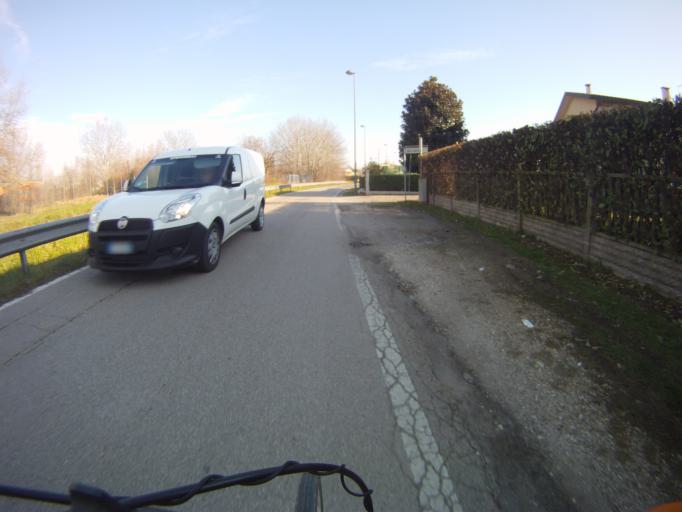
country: IT
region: Veneto
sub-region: Provincia di Padova
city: Piove di Sacco-Piovega
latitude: 45.2951
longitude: 12.0260
